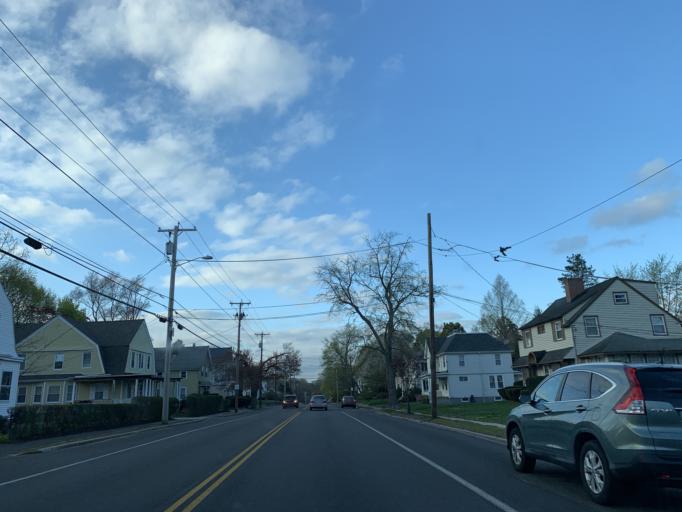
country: US
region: Rhode Island
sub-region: Providence County
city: Central Falls
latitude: 41.8887
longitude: -71.4127
